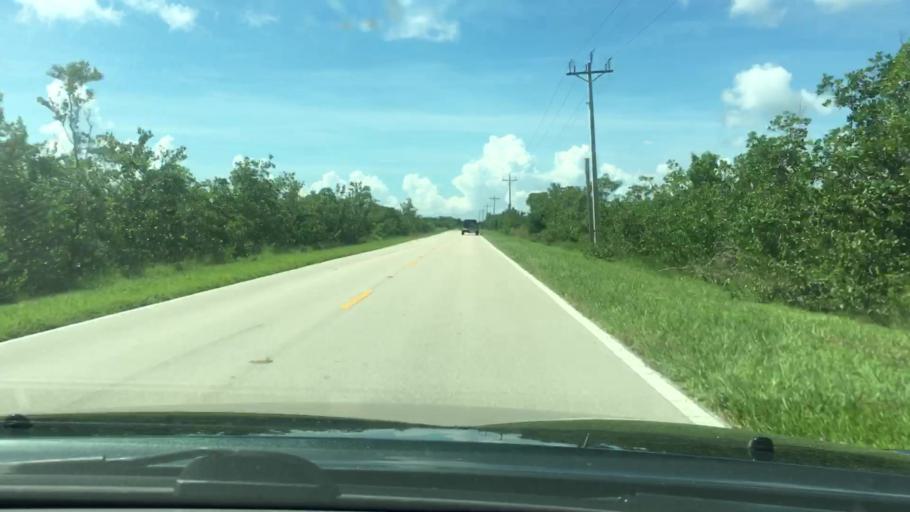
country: US
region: Florida
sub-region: Collier County
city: Marco
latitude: 25.9449
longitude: -81.6441
